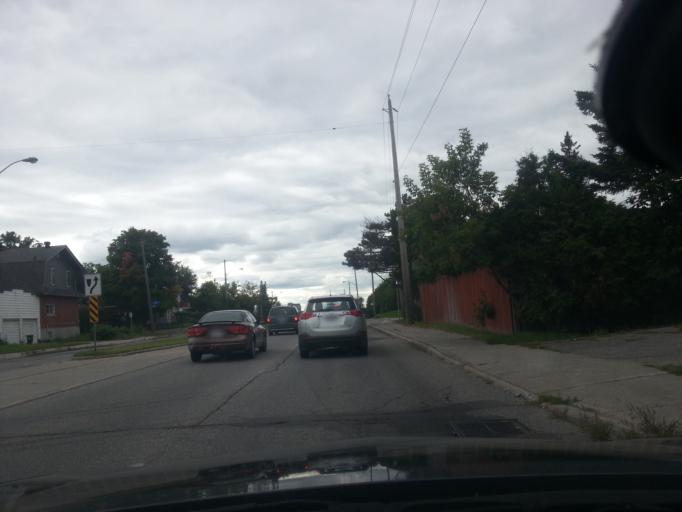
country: CA
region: Ontario
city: Ottawa
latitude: 45.3790
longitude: -75.6634
